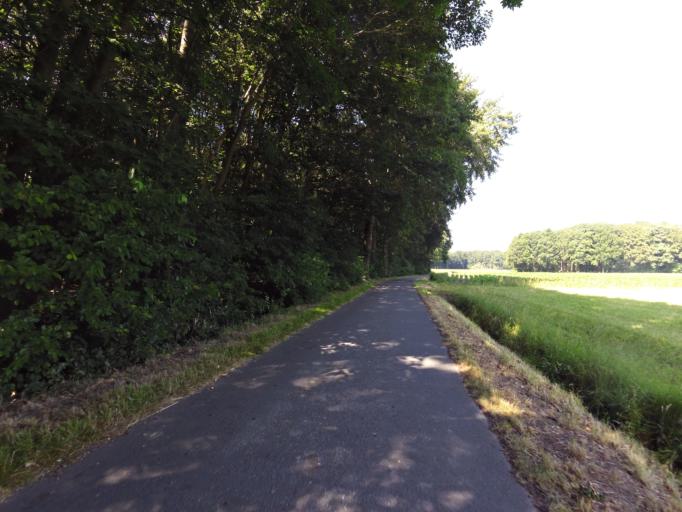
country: BE
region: Flanders
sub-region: Provincie West-Vlaanderen
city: Zedelgem
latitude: 51.1553
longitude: 3.1408
